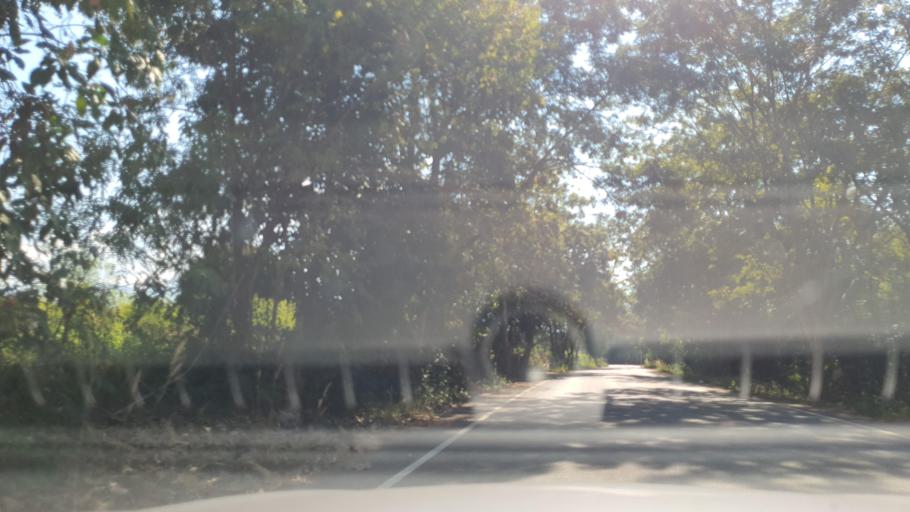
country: TH
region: Nan
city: Pua
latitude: 19.1523
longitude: 100.9088
